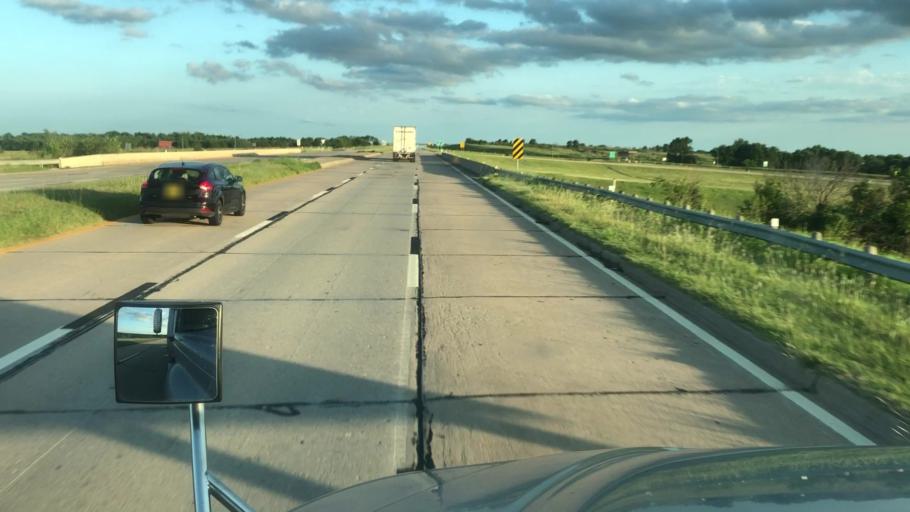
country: US
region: Oklahoma
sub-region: Pawnee County
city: Pawnee
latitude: 36.2988
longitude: -96.9874
